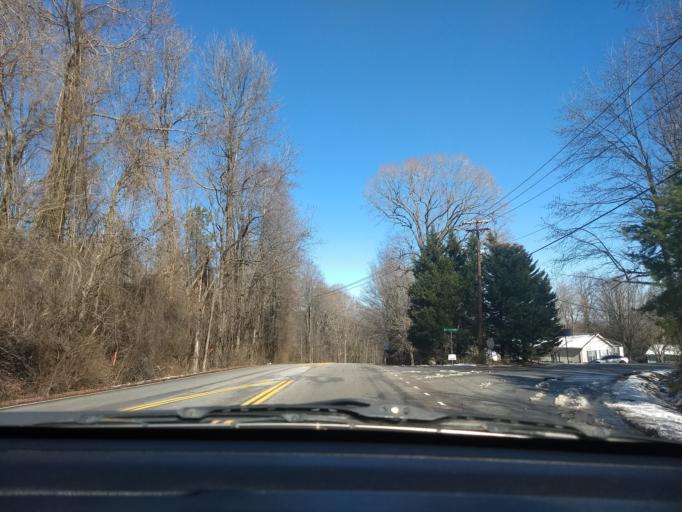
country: US
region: South Carolina
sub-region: Greenville County
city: Sans Souci
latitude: 34.9050
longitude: -82.3864
